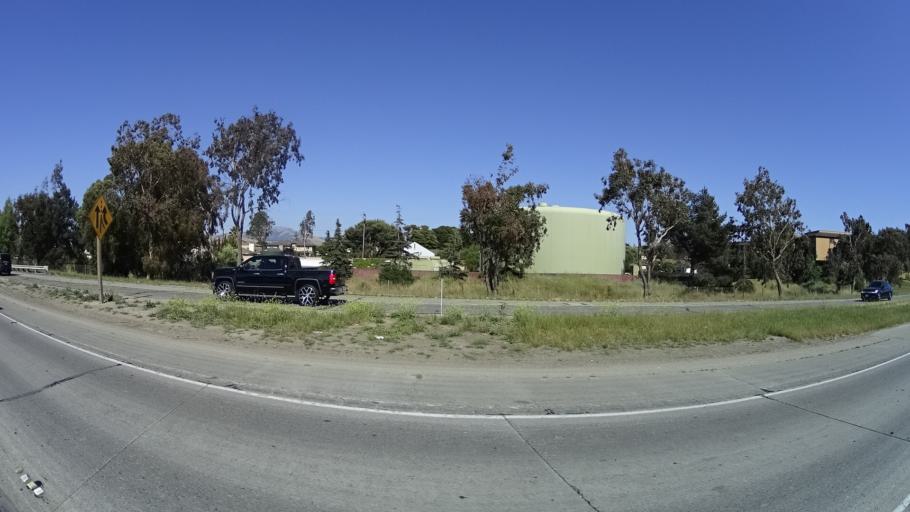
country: US
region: California
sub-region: Monterey County
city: Boronda
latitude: 36.7246
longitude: -121.6590
